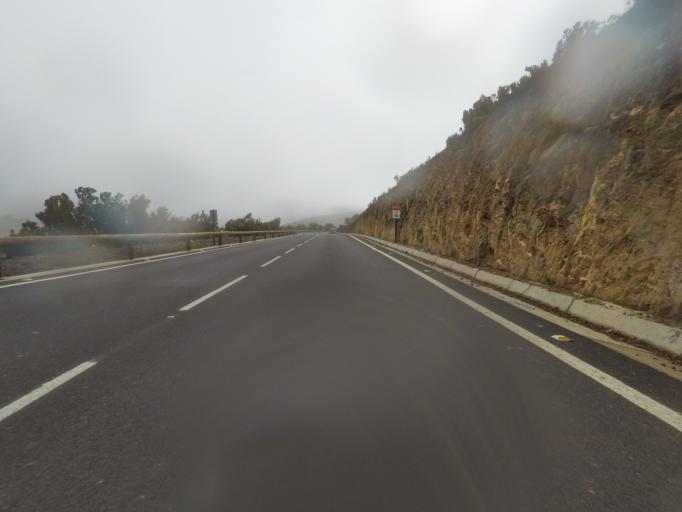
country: ES
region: Canary Islands
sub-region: Provincia de Santa Cruz de Tenerife
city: Vallehermosa
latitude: 28.1466
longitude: -17.3084
